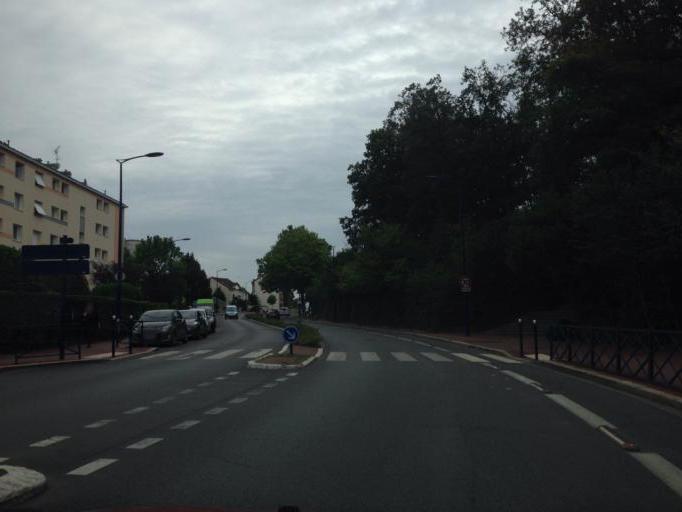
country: FR
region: Ile-de-France
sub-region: Departement des Hauts-de-Seine
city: Le Plessis-Robinson
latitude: 48.7926
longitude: 2.2647
